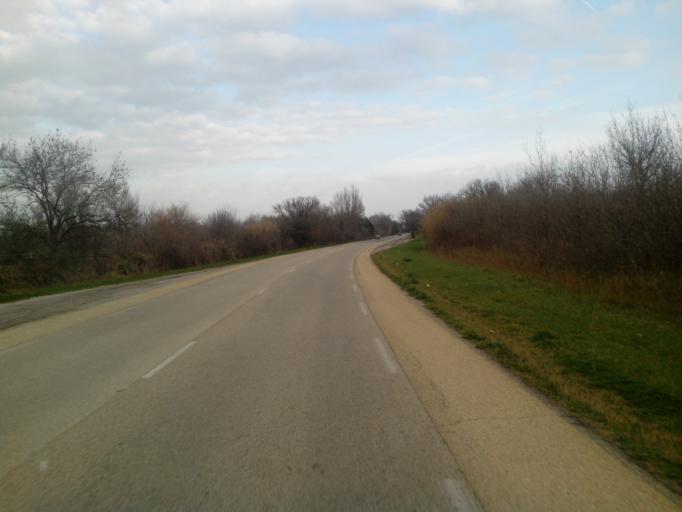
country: FR
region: Provence-Alpes-Cote d'Azur
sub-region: Departement des Bouches-du-Rhone
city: Saintes-Maries-de-la-Mer
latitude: 43.5518
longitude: 4.4043
